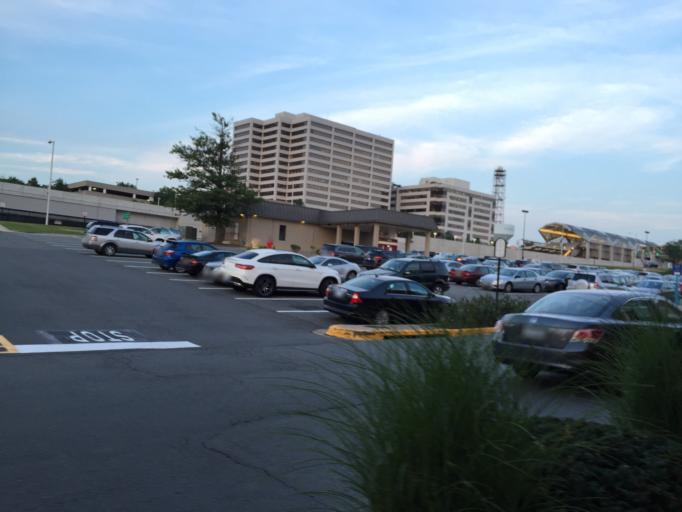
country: US
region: Virginia
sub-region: Fairfax County
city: Tysons Corner
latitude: 38.9222
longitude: -77.2367
